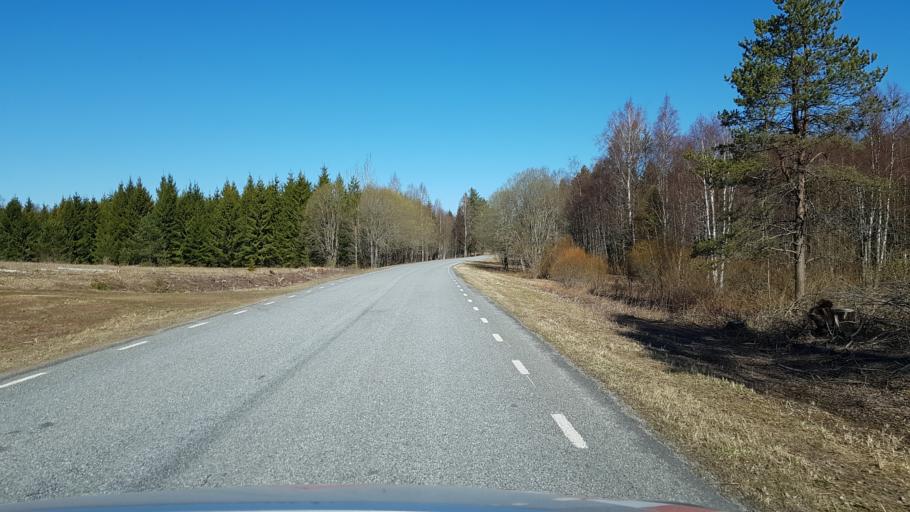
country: EE
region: Laeaene-Virumaa
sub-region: Haljala vald
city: Haljala
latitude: 59.4986
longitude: 26.2407
